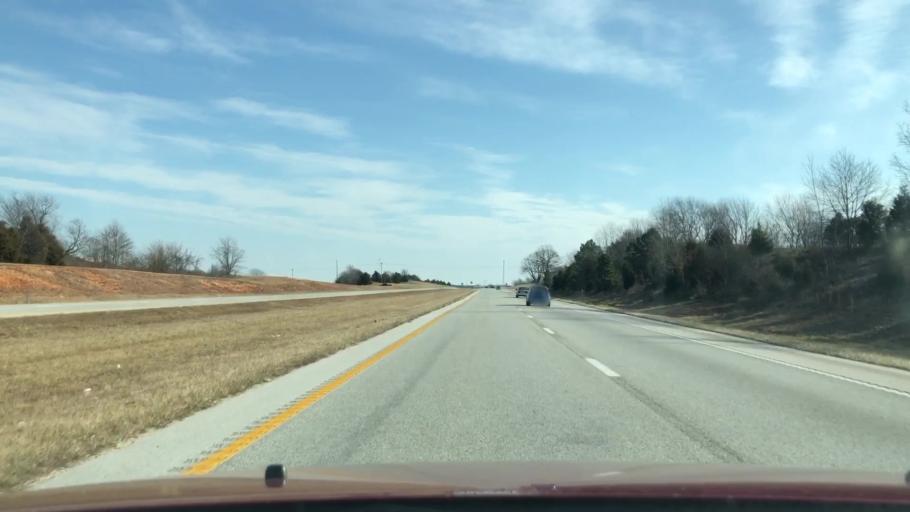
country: US
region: Missouri
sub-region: Webster County
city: Seymour
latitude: 37.1564
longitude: -92.7769
